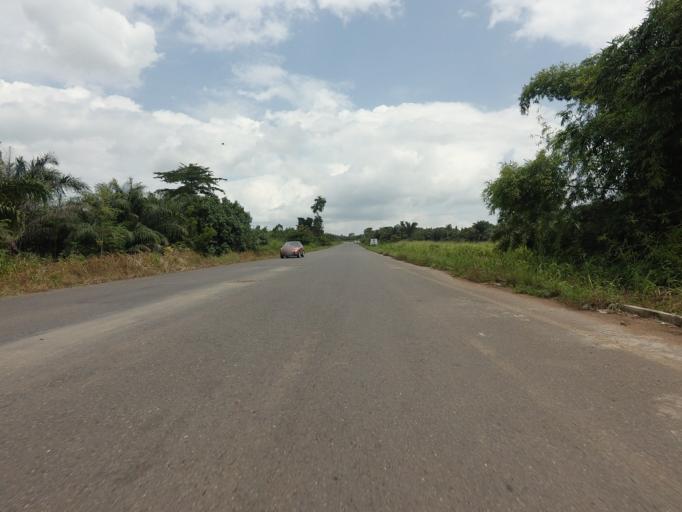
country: GH
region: Volta
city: Ho
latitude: 6.5254
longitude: 0.2232
